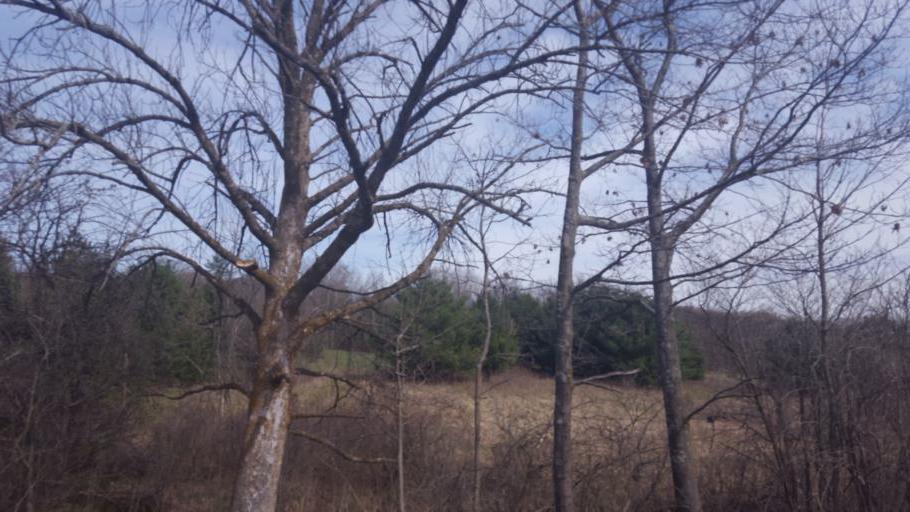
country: US
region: Michigan
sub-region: Gladwin County
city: Gladwin
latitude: 44.0203
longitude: -84.5248
